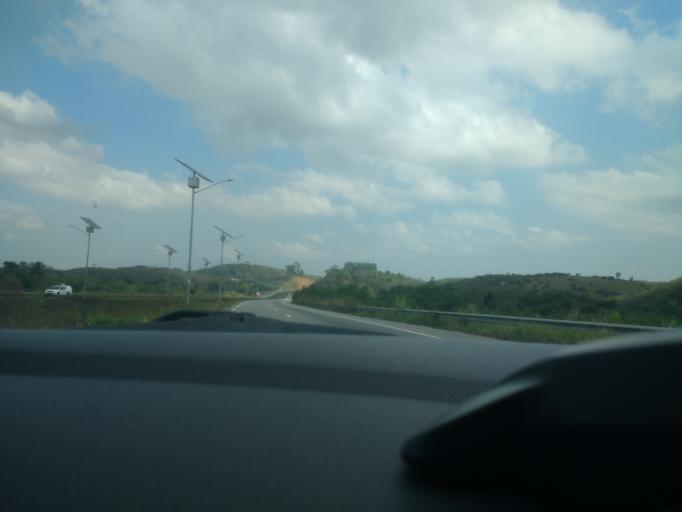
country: BR
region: Rio de Janeiro
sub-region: Queimados
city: Queimados
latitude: -22.6621
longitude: -43.5828
